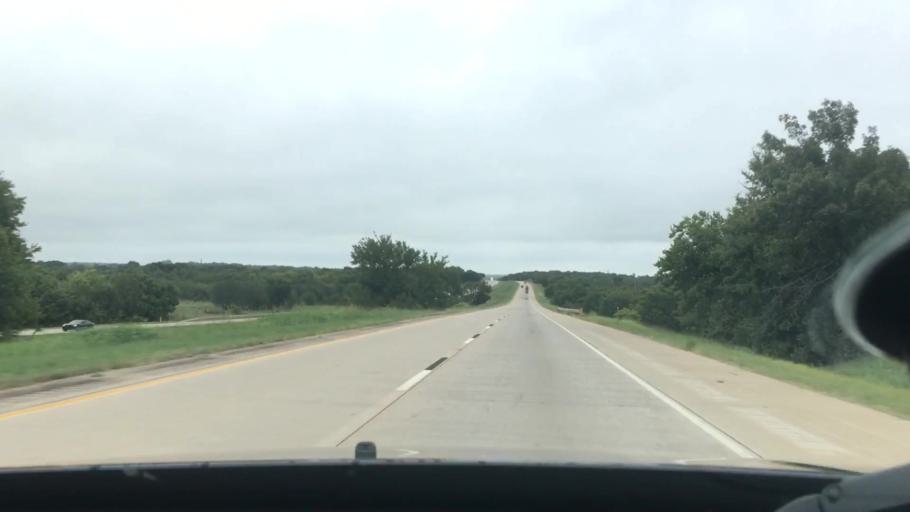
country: US
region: Oklahoma
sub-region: Okfuskee County
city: Okemah
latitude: 35.4280
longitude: -96.1720
